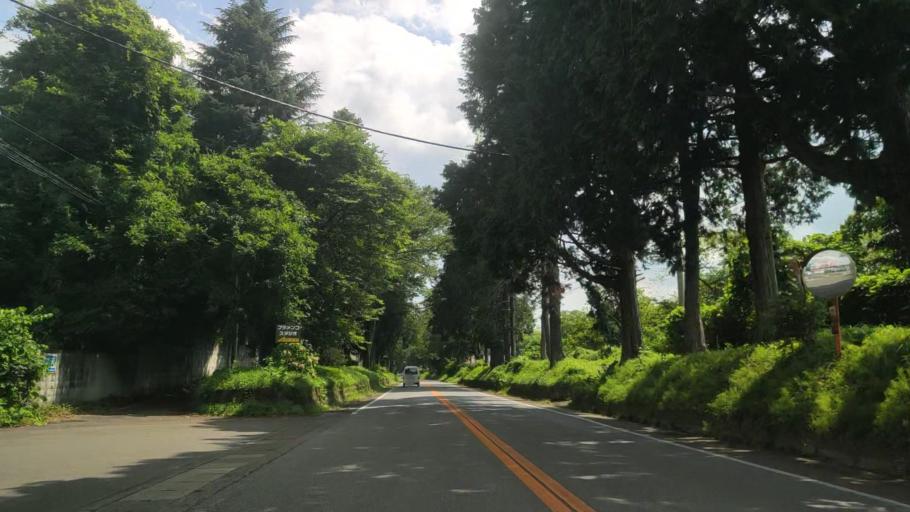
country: JP
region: Tochigi
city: Utsunomiya-shi
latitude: 36.6152
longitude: 139.8538
